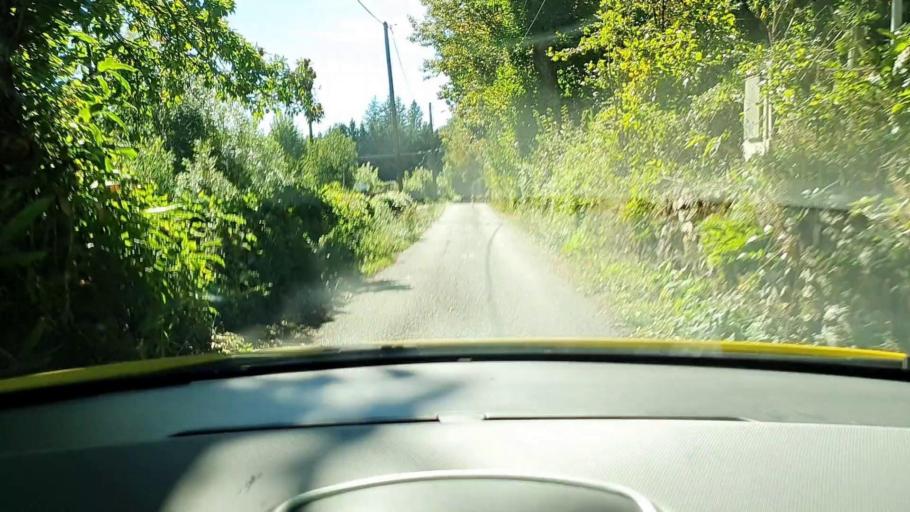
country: FR
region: Languedoc-Roussillon
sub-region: Departement du Gard
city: Le Vigan
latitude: 43.9836
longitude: 3.4458
